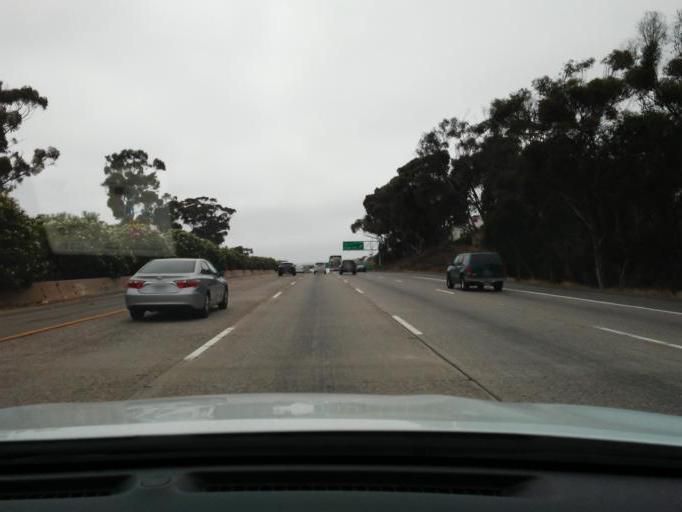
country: US
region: California
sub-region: San Diego County
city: Oceanside
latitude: 33.2020
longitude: -117.3766
